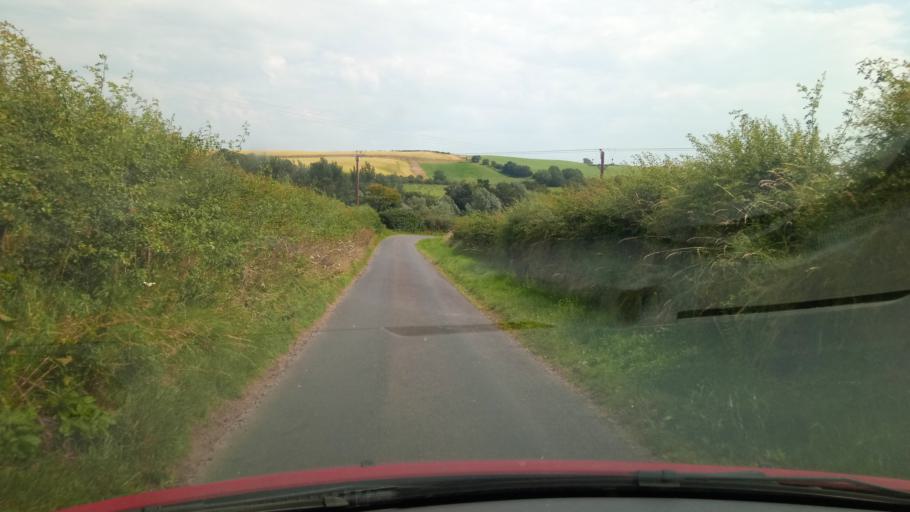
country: GB
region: Scotland
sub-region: The Scottish Borders
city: Kelso
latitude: 55.5752
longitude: -2.4730
